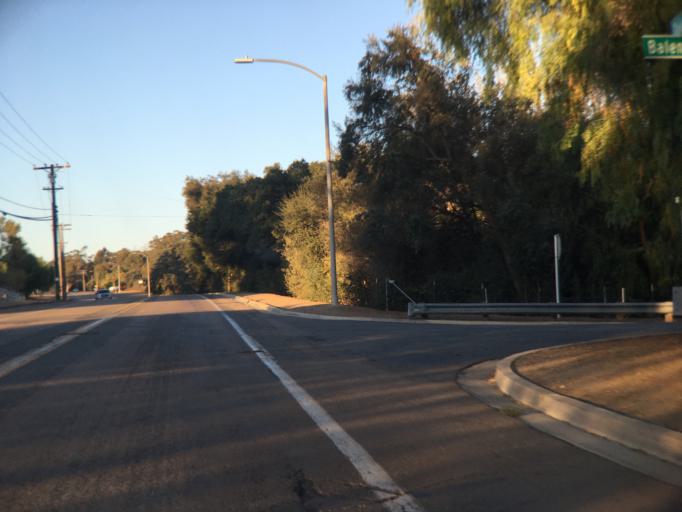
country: US
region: California
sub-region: San Diego County
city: Alpine
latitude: 32.8099
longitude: -116.7799
